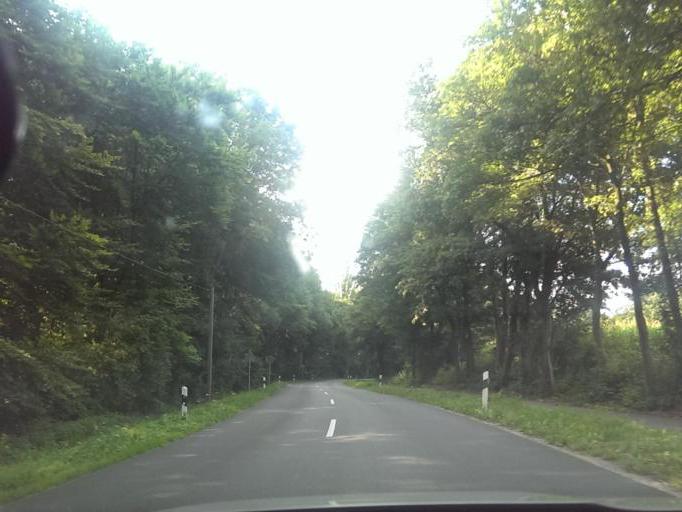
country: DE
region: North Rhine-Westphalia
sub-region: Regierungsbezirk Detmold
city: Delbruck
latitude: 51.7534
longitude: 8.5082
